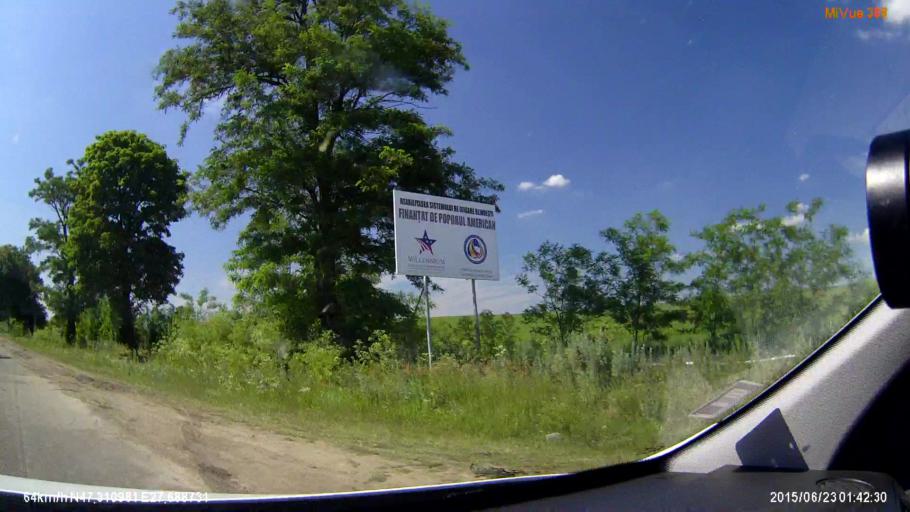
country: RO
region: Iasi
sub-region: Comuna Golaesti
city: Golaesti
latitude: 47.3109
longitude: 27.6889
